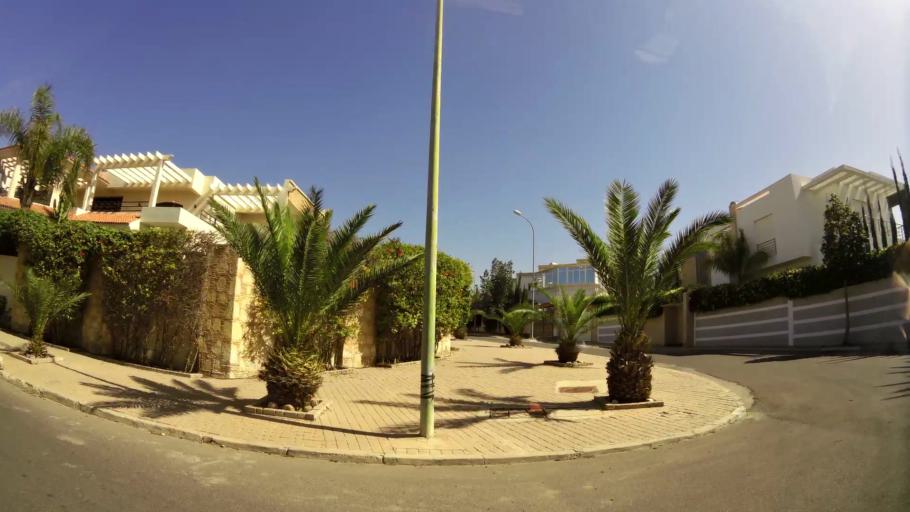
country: MA
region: Souss-Massa-Draa
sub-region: Agadir-Ida-ou-Tnan
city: Agadir
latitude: 30.4423
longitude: -9.5813
